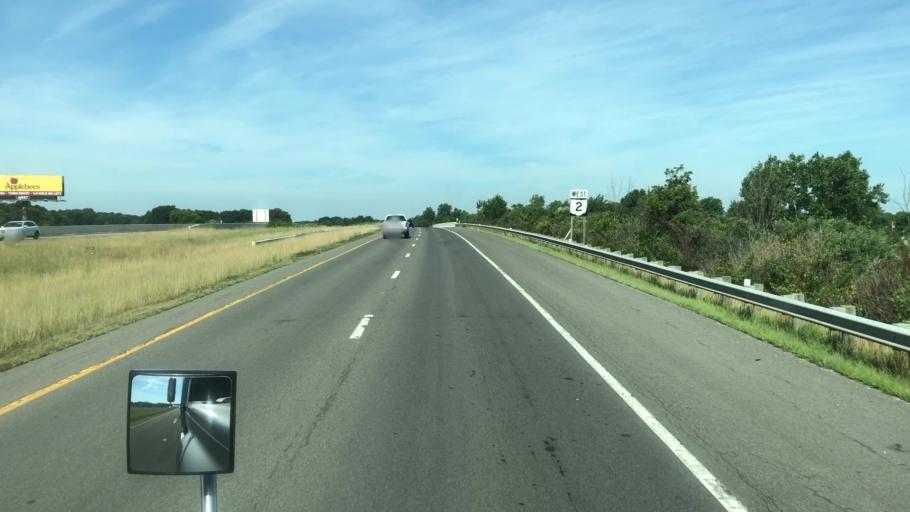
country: US
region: Ohio
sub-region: Erie County
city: Huron
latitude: 41.4060
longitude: -82.6013
